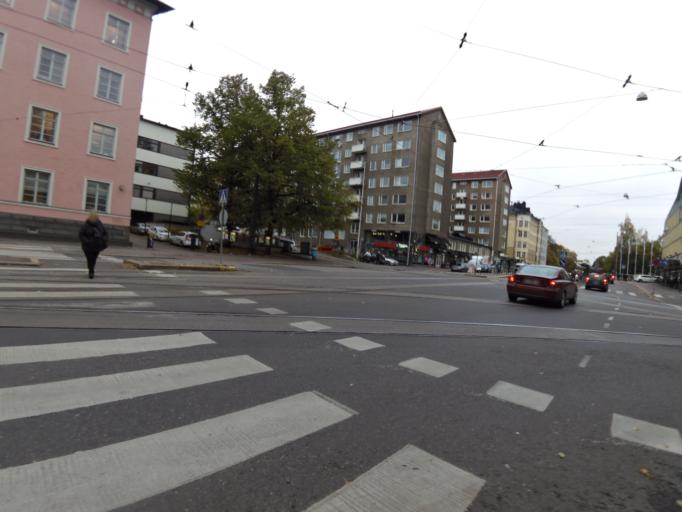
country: FI
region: Uusimaa
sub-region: Helsinki
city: Helsinki
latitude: 60.1866
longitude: 24.9490
